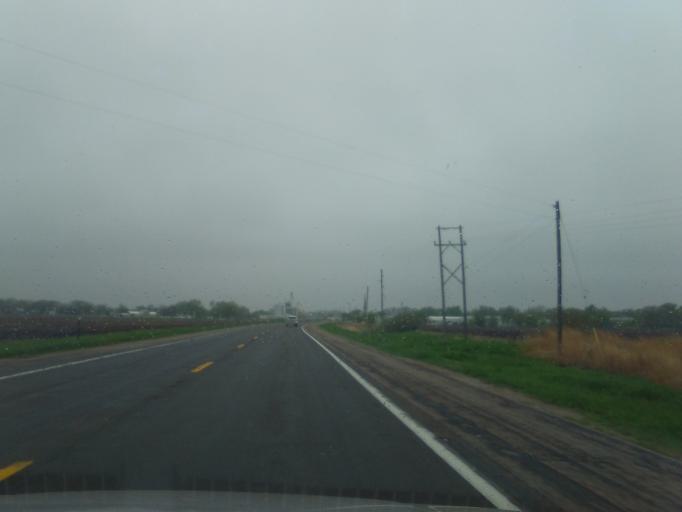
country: US
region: Nebraska
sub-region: Cuming County
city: West Point
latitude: 41.9224
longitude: -96.8016
